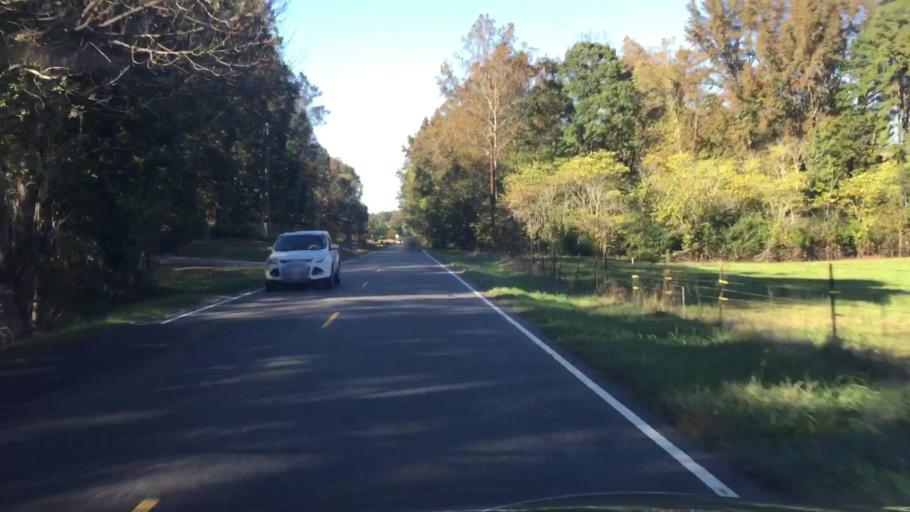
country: US
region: North Carolina
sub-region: Gaston County
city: Davidson
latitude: 35.5132
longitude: -80.7693
